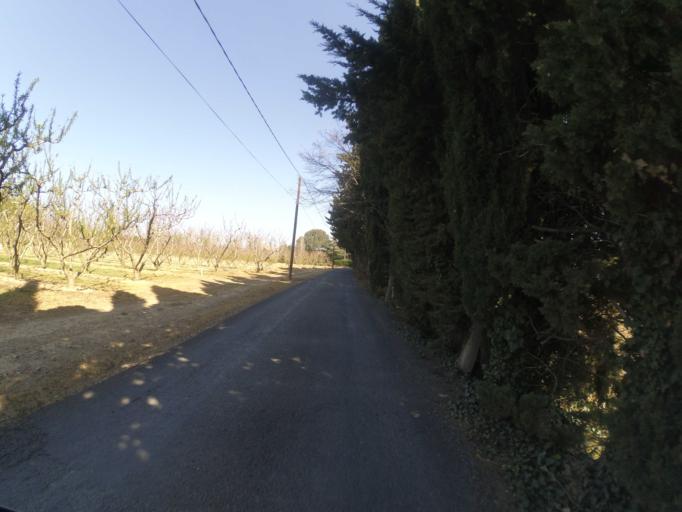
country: FR
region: Languedoc-Roussillon
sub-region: Departement des Pyrenees-Orientales
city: Pezilla-la-Riviere
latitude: 42.6711
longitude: 2.7616
